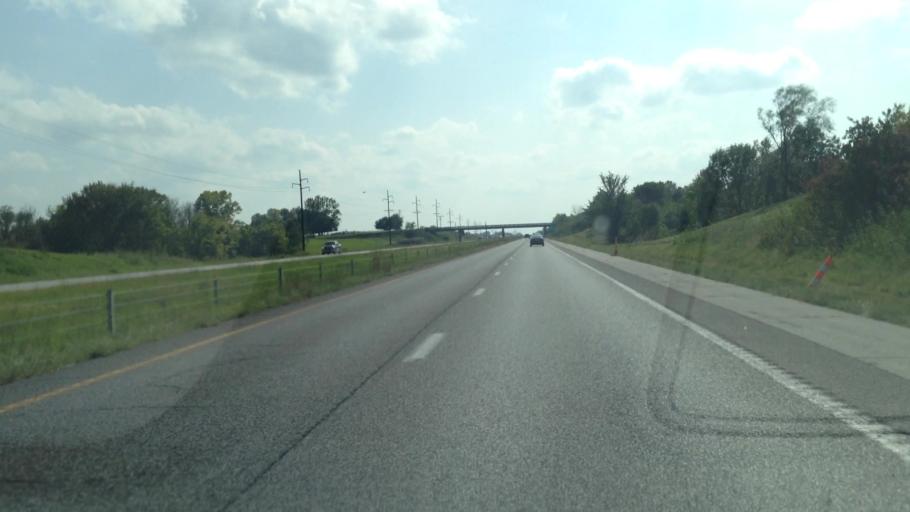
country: US
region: Missouri
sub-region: Clay County
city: Kearney
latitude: 39.3284
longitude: -94.3937
